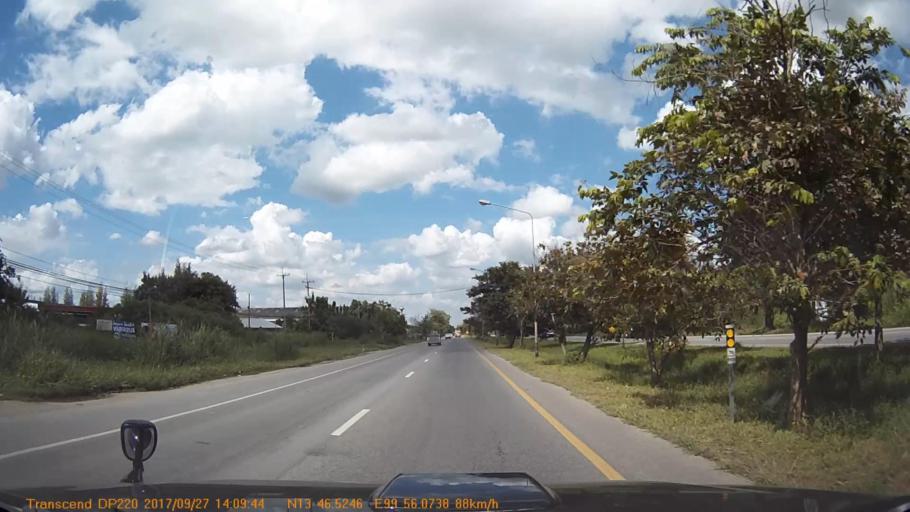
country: TH
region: Ratchaburi
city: Ban Pong
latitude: 13.7752
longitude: 99.9345
